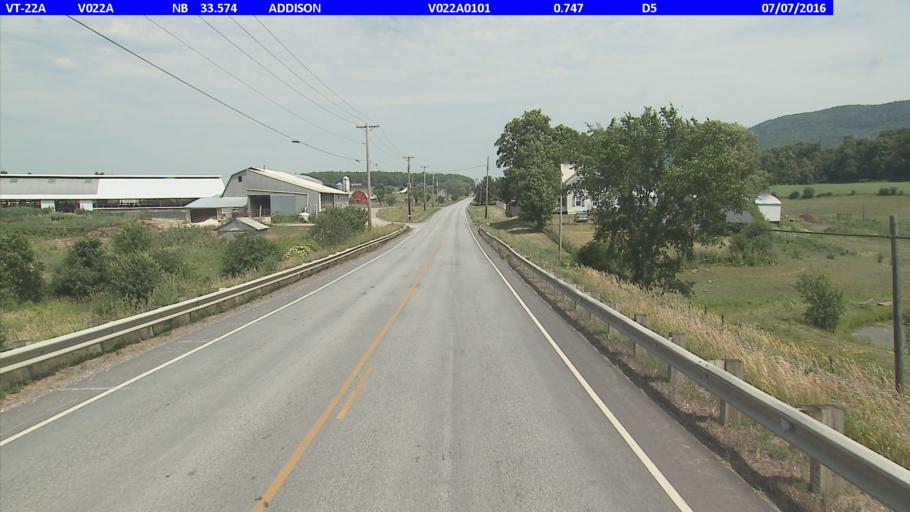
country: US
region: Vermont
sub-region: Addison County
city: Vergennes
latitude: 44.0406
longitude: -73.3055
